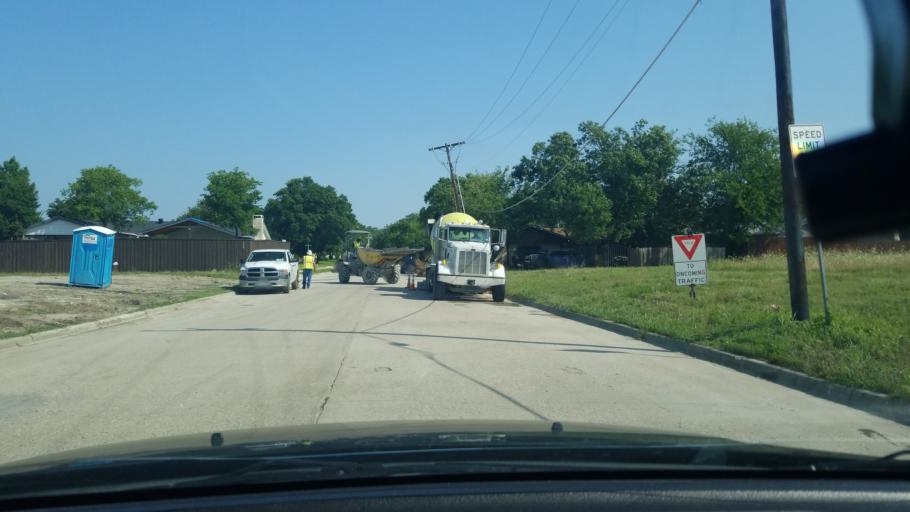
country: US
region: Texas
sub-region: Dallas County
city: Mesquite
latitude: 32.8156
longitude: -96.6451
